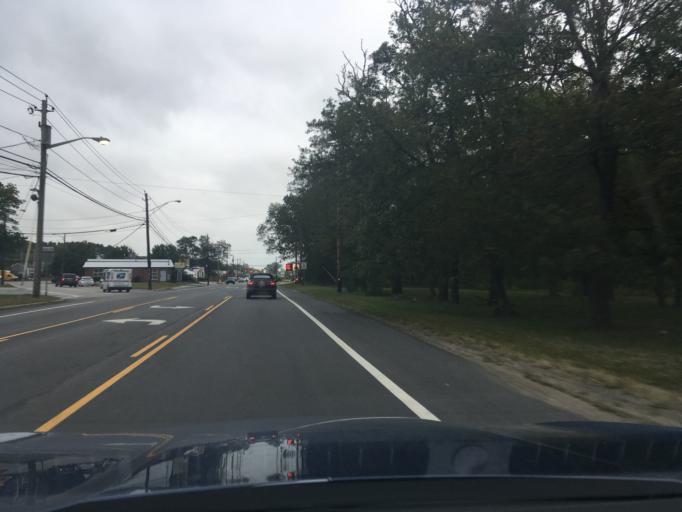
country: US
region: Rhode Island
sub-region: Washington County
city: North Kingstown
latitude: 41.5848
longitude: -71.4589
